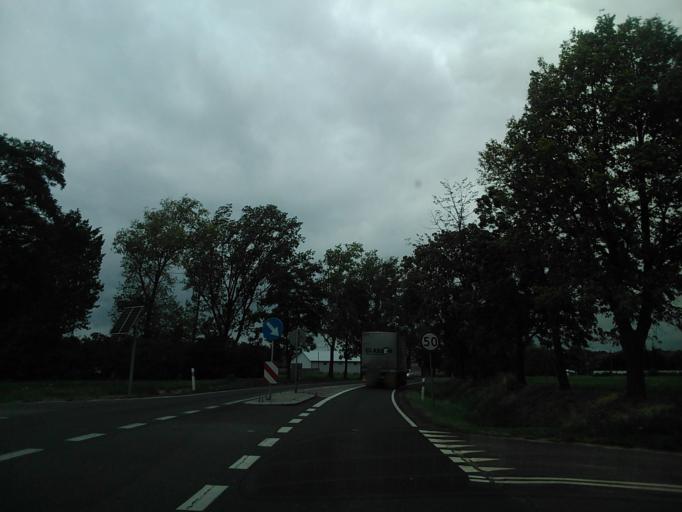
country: PL
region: Kujawsko-Pomorskie
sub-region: Powiat inowroclawski
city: Kruszwica
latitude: 52.6371
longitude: 18.3846
